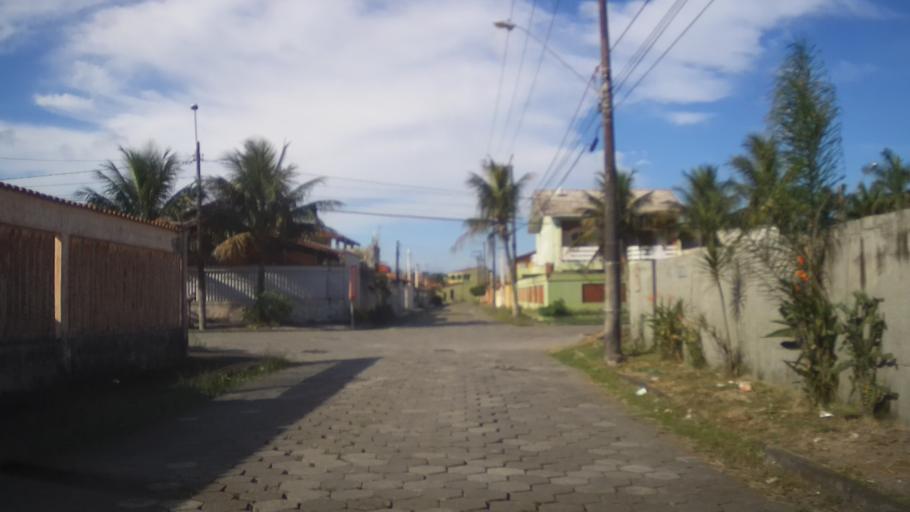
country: BR
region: Sao Paulo
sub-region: Itanhaem
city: Itanhaem
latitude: -24.1571
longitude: -46.7382
